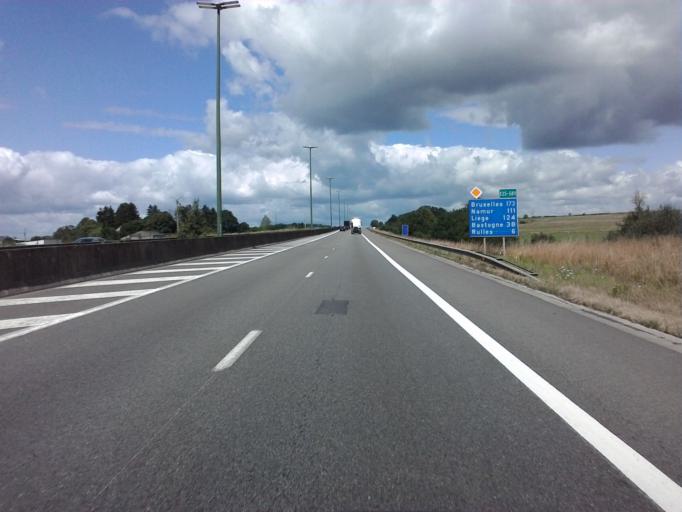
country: BE
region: Wallonia
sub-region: Province du Luxembourg
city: Habay-la-Vieille
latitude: 49.7093
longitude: 5.6168
